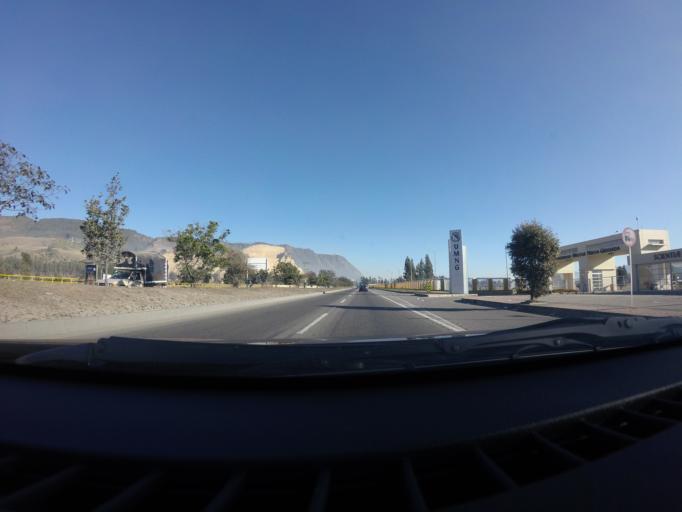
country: CO
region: Cundinamarca
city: Cajica
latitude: 4.9451
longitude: -74.0154
